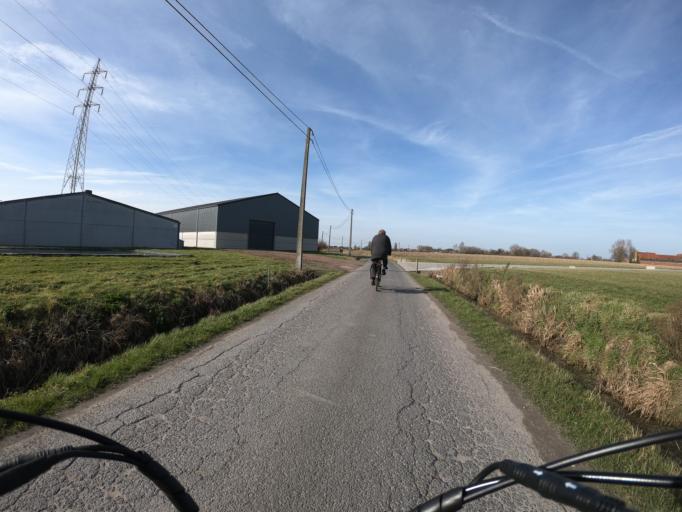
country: BE
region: Flanders
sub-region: Provincie West-Vlaanderen
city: Menen
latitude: 50.8205
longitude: 3.1274
